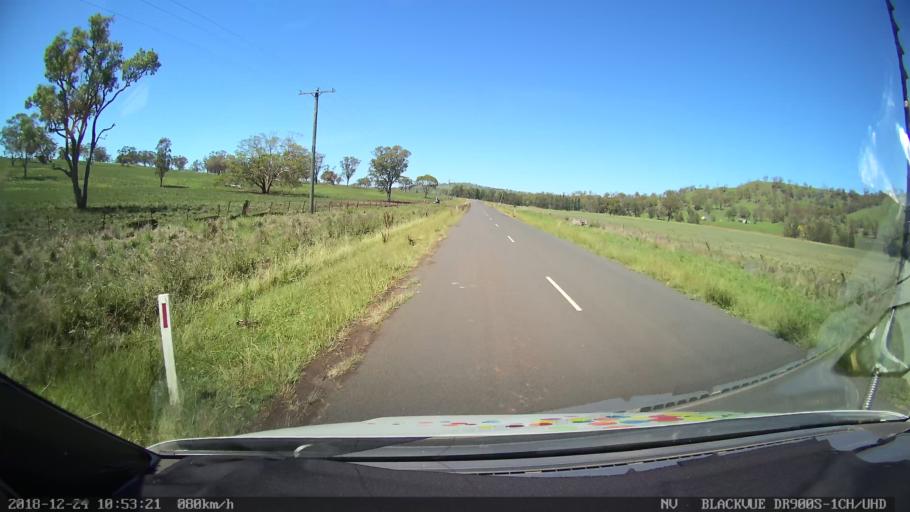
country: AU
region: New South Wales
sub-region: Upper Hunter Shire
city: Merriwa
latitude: -31.9907
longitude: 150.4215
